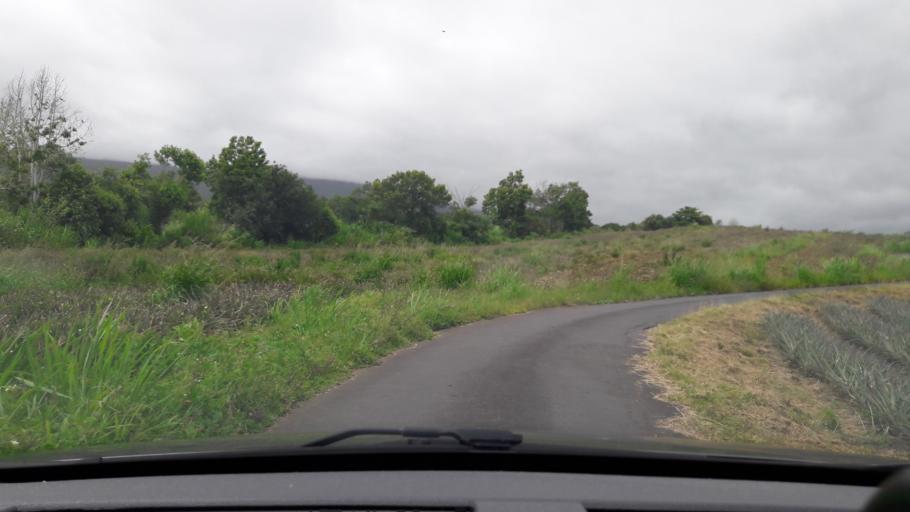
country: RE
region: Reunion
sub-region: Reunion
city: Saint-Benoit
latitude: -21.0956
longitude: 55.7015
